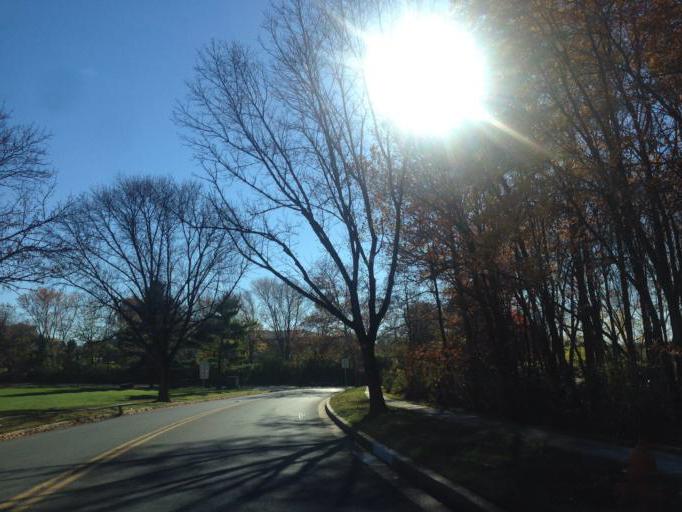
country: US
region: Maryland
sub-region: Howard County
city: Riverside
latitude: 39.1934
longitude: -76.8714
